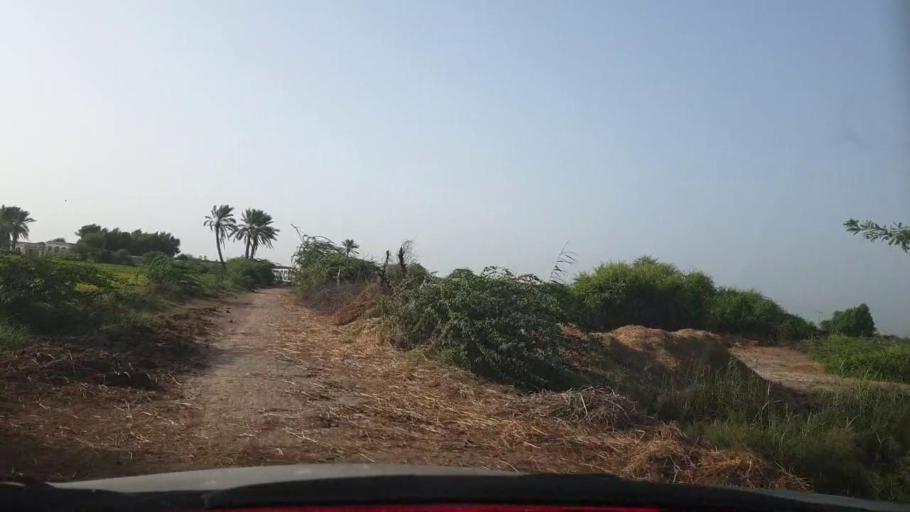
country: PK
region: Sindh
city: Talhar
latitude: 24.9039
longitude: 68.8212
